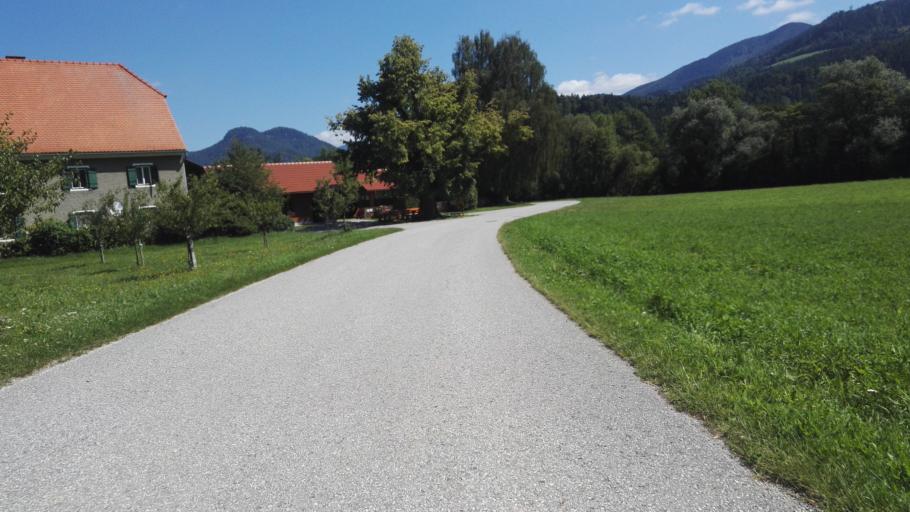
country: AT
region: Styria
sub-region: Politischer Bezirk Graz-Umgebung
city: Frohnleiten
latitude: 47.2429
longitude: 15.3101
